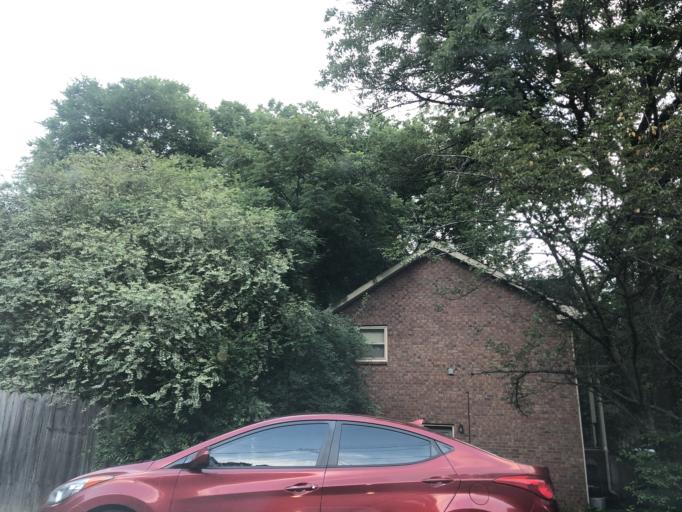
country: US
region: Tennessee
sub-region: Davidson County
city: Lakewood
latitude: 36.1465
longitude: -86.6365
